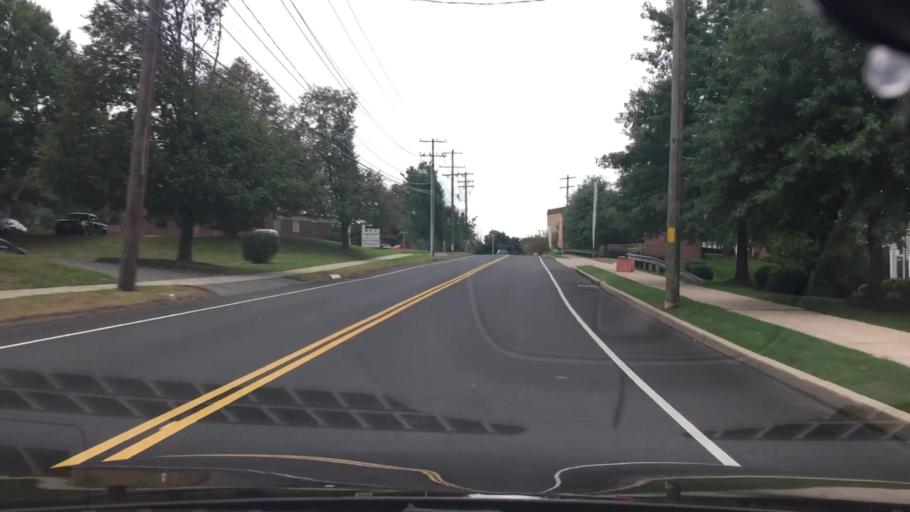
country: US
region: Connecticut
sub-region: New Haven County
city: Meriden
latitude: 41.5213
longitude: -72.7638
